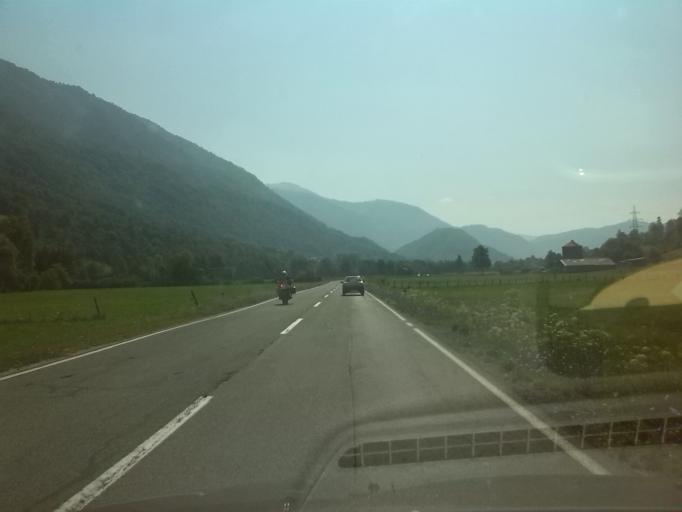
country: SI
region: Tolmin
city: Tolmin
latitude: 46.2039
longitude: 13.6784
